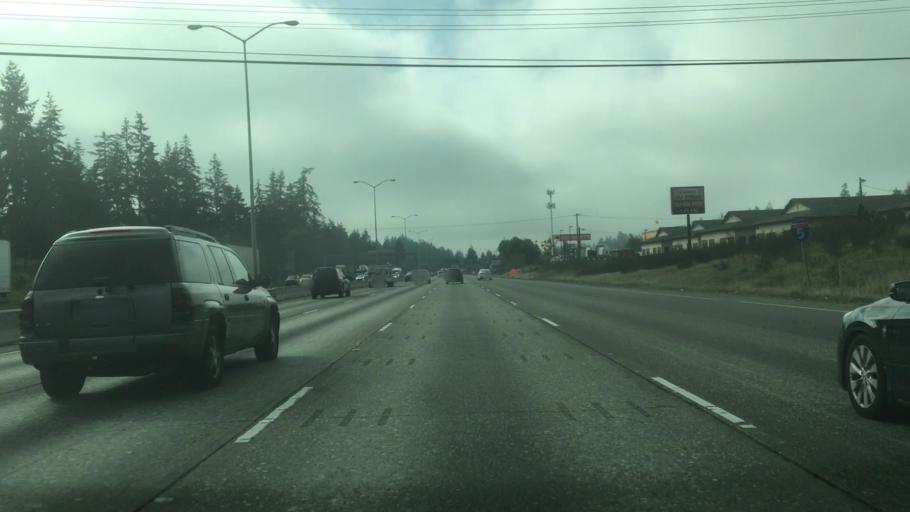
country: US
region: Washington
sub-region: Pierce County
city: McChord Air Force Base
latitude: 47.1447
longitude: -122.5092
